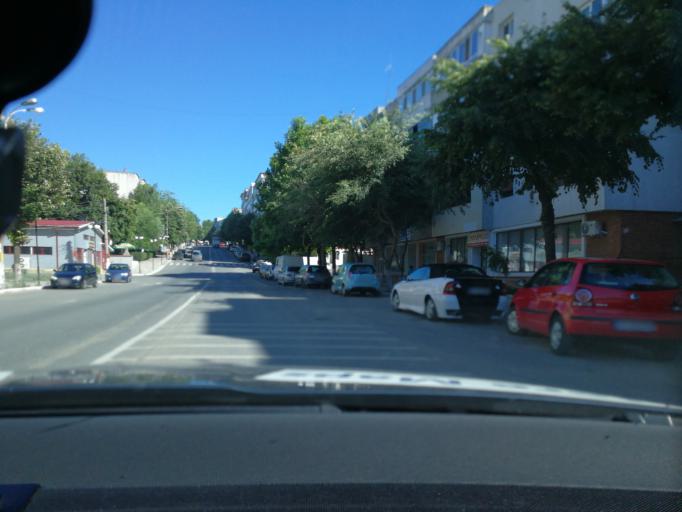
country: RO
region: Tulcea
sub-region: Oras Macin
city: Macin
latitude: 45.2468
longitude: 28.1280
